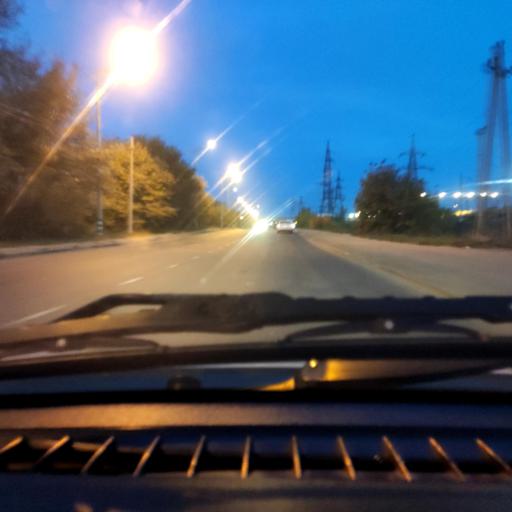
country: RU
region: Samara
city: Zhigulevsk
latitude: 53.4781
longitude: 49.5206
